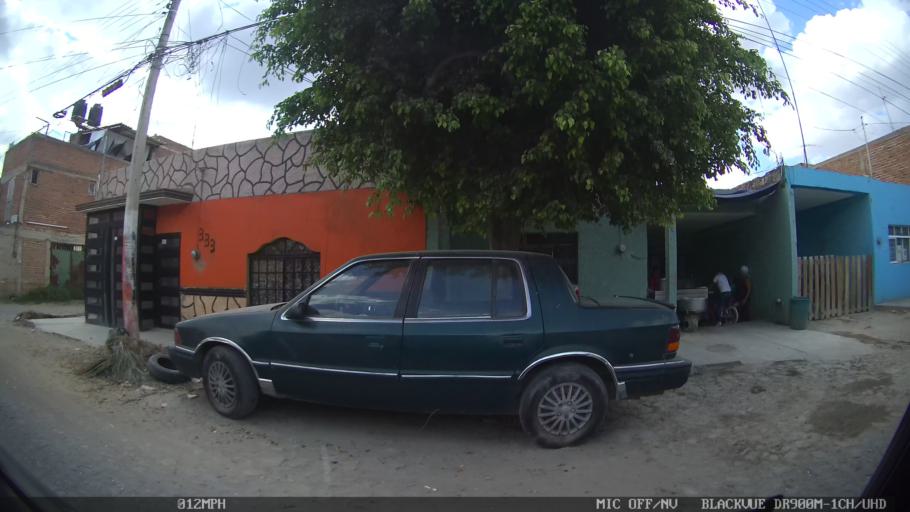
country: MX
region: Jalisco
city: Tonala
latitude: 20.6559
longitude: -103.2534
